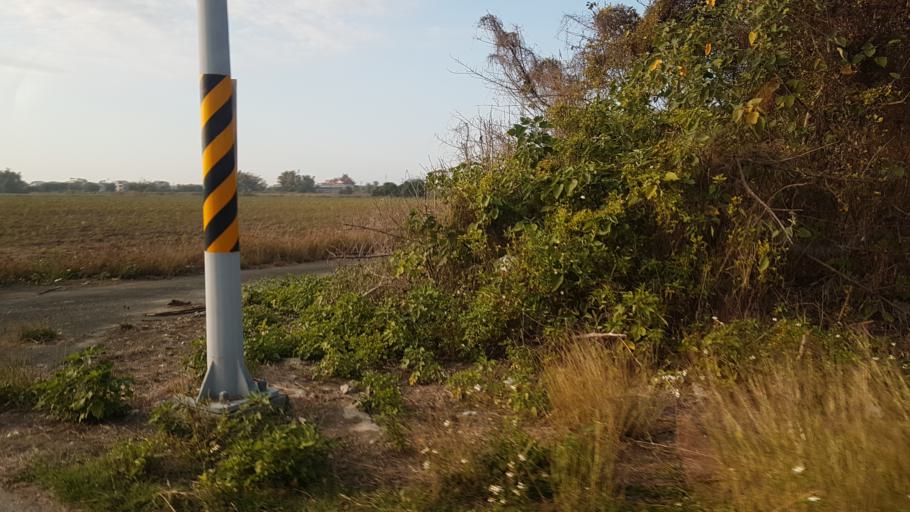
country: TW
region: Taiwan
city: Xinying
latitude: 23.3463
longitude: 120.3738
